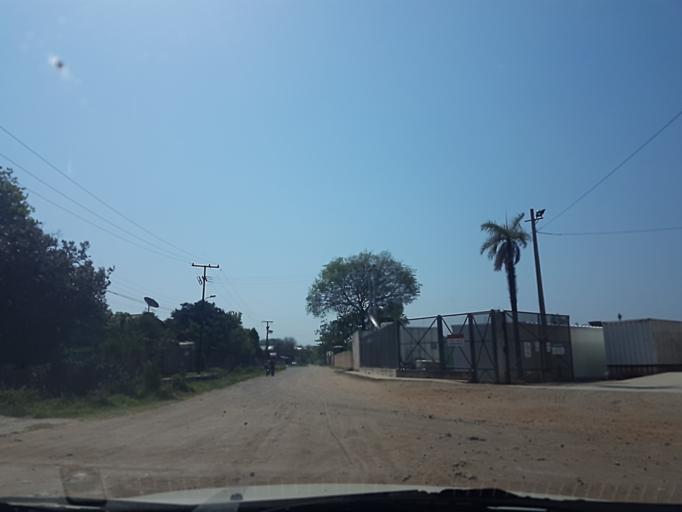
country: PY
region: Central
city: Colonia Mariano Roque Alonso
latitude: -25.2048
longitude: -57.5320
